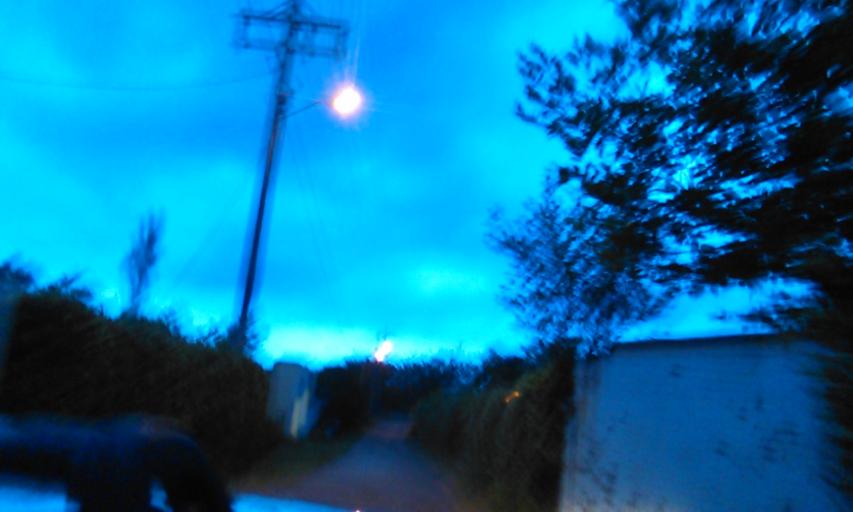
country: CO
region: Quindio
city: La Tebaida
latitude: 4.4946
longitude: -75.8593
